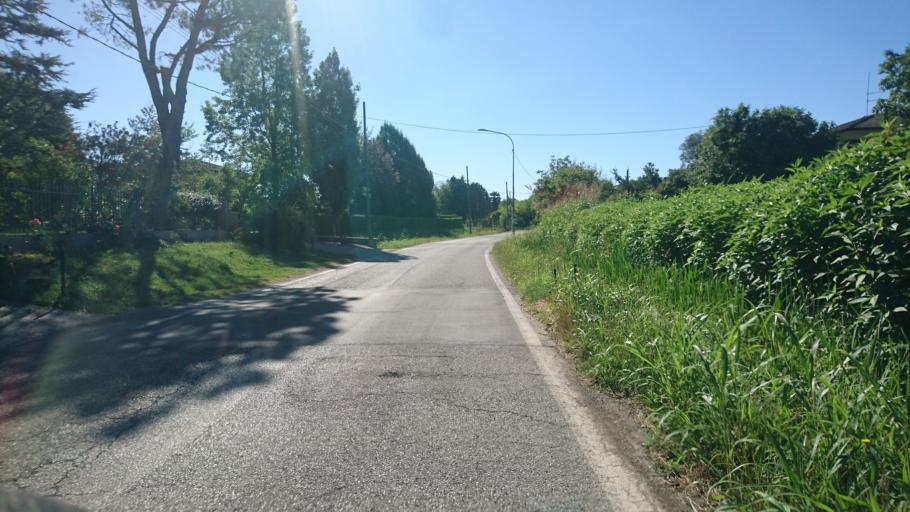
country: IT
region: Veneto
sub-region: Provincia di Padova
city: Legnaro
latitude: 45.3313
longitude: 11.9701
